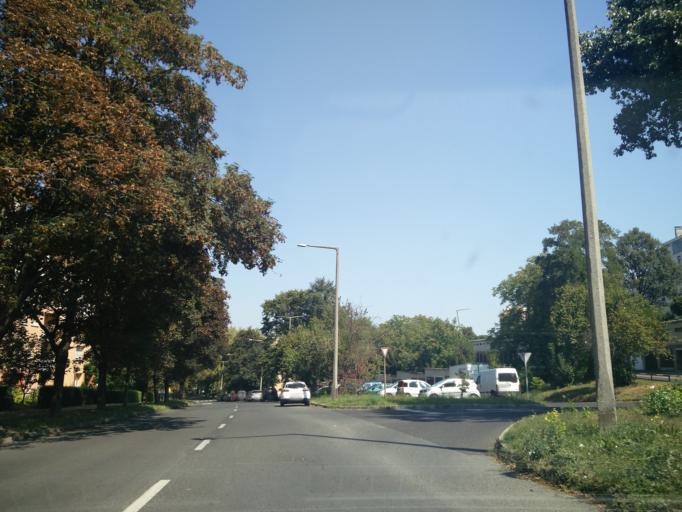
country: HU
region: Zala
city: Zalaegerszeg
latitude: 46.8360
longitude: 16.8253
